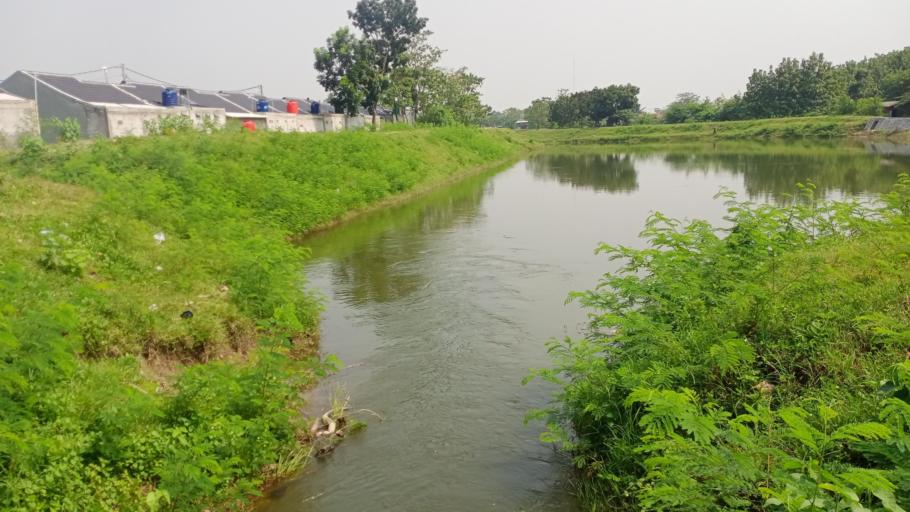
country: ID
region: West Java
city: Cileungsir
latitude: -6.3792
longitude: 107.0903
